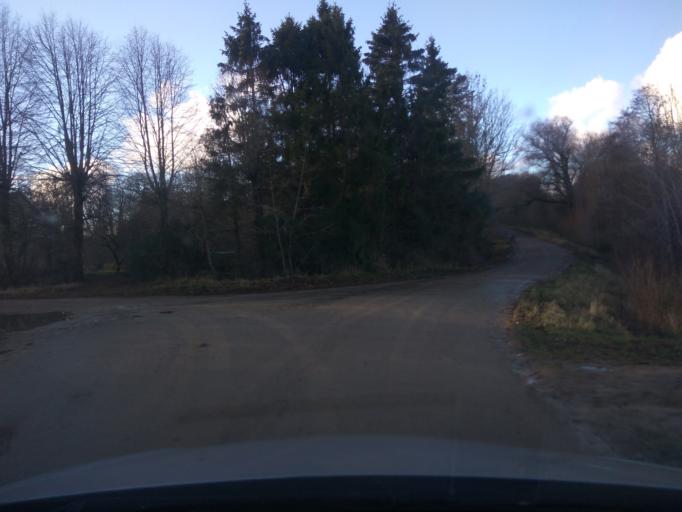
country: LV
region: Aizpute
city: Aizpute
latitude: 56.7479
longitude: 21.5904
